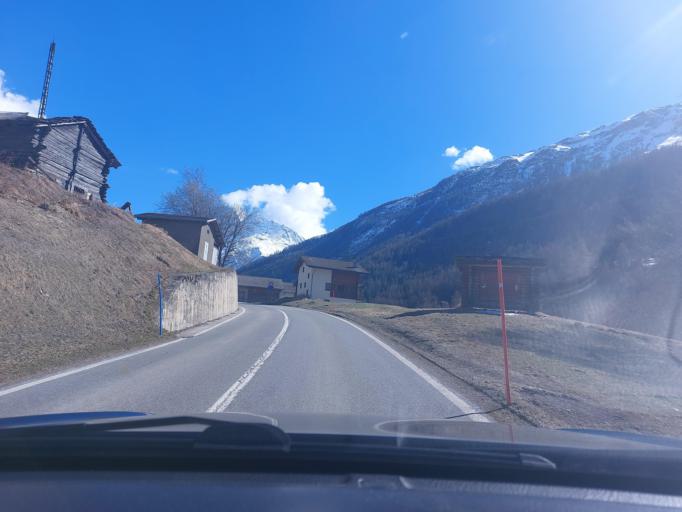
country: CH
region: Valais
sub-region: Herens District
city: Evolene
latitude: 46.1219
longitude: 7.4842
